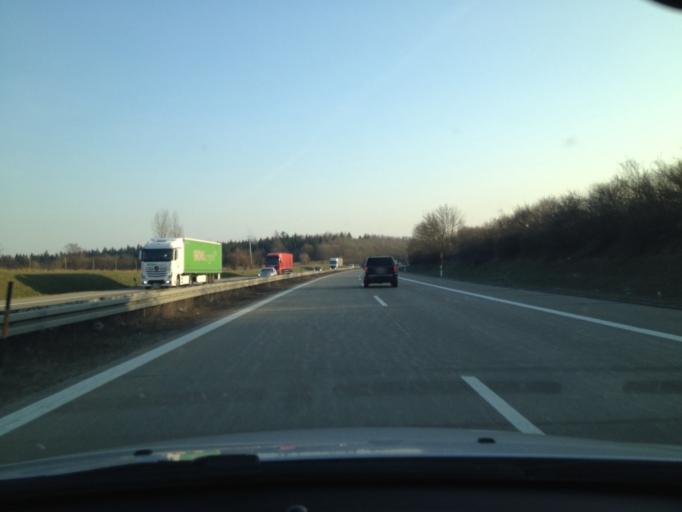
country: DE
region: Baden-Wuerttemberg
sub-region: Regierungsbezirk Stuttgart
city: Lauchheim
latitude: 48.8227
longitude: 10.2164
